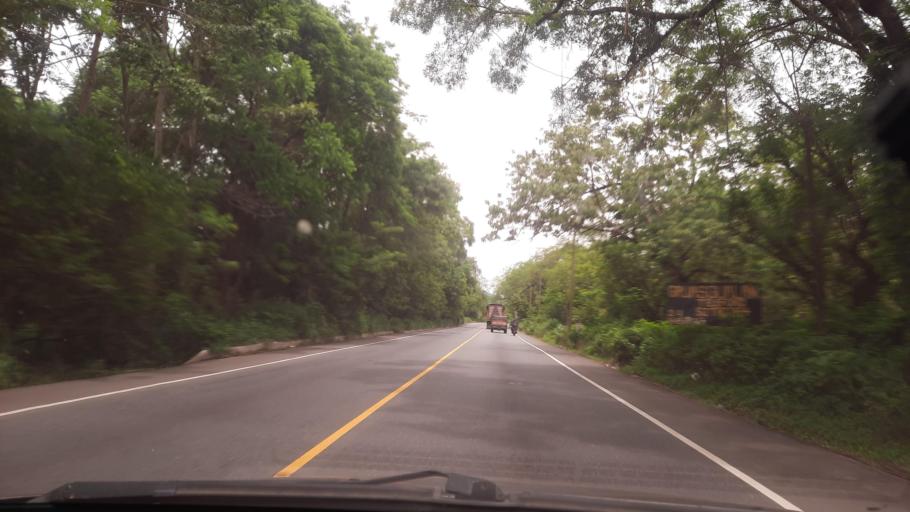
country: GT
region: Izabal
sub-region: Municipio de Los Amates
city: Los Amates
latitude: 15.2179
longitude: -89.2263
